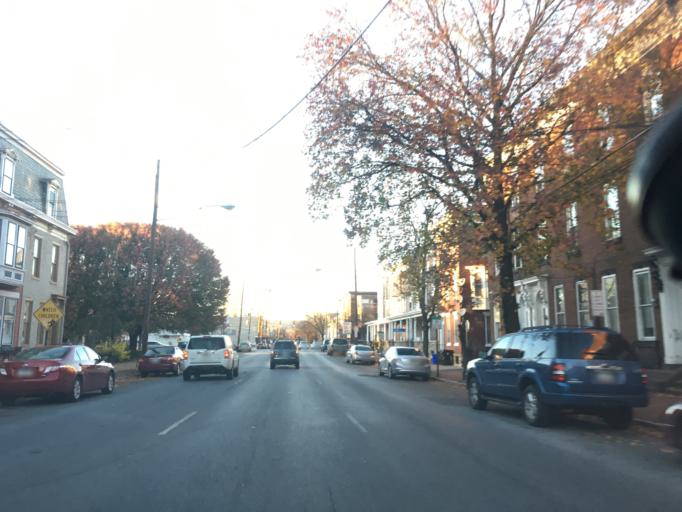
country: US
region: Pennsylvania
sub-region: Dauphin County
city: Harrisburg
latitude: 40.2677
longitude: -76.8909
